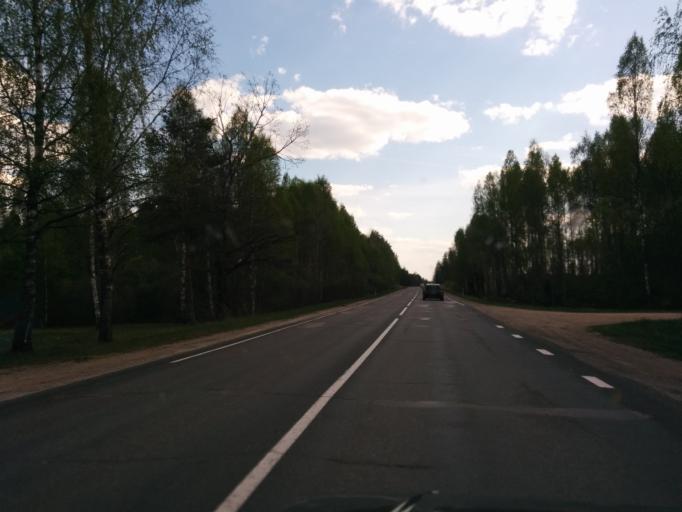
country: LV
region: Pargaujas
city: Stalbe
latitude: 57.3156
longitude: 24.9232
